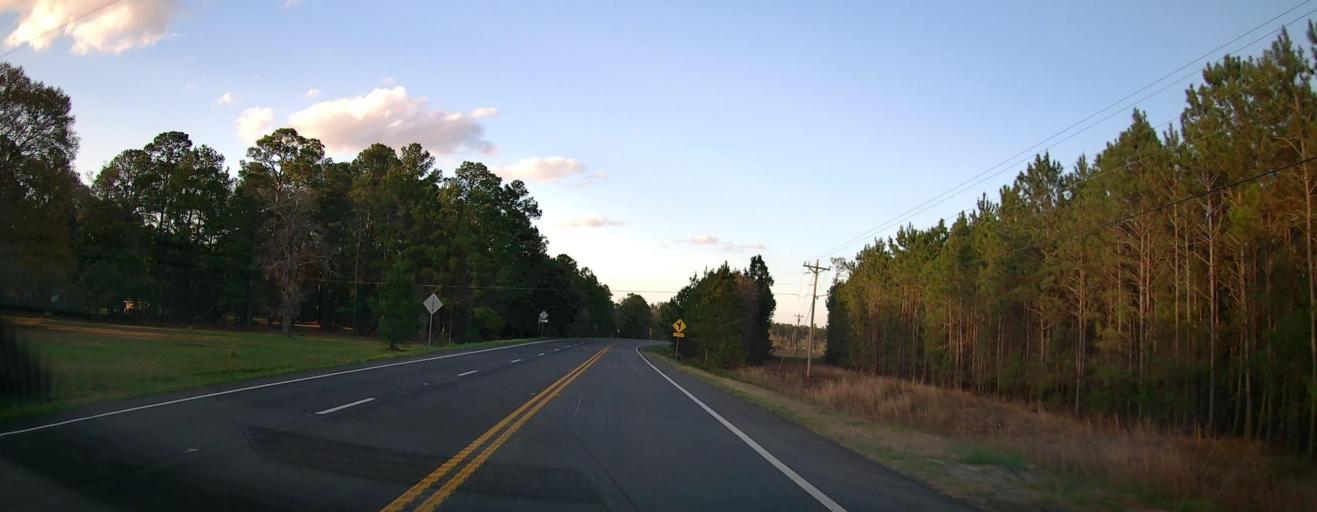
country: US
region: Georgia
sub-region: Bryan County
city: Pembroke
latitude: 32.1338
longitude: -81.5365
